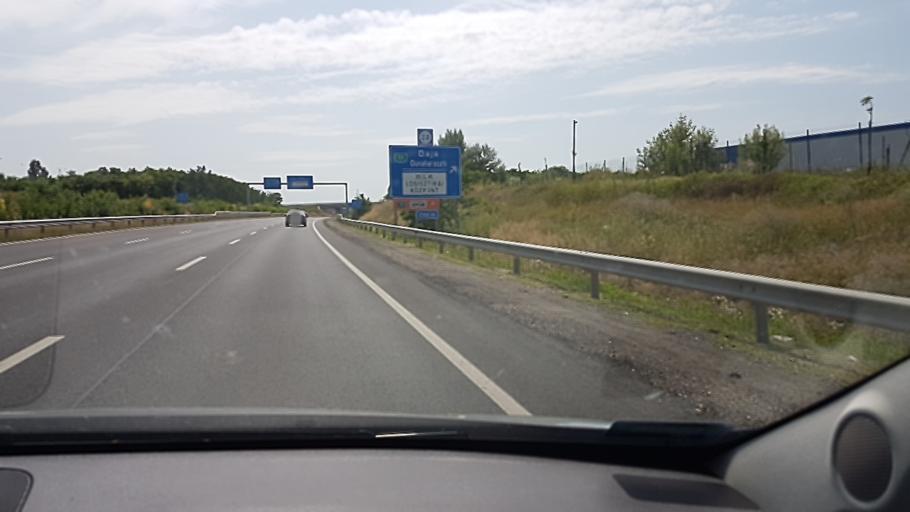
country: HU
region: Budapest
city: Budapest XXIII. keruelet
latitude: 47.3718
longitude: 19.1275
